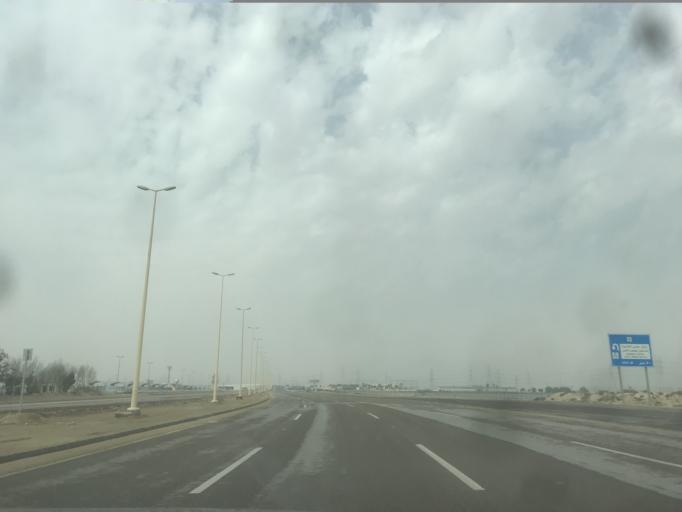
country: SA
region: Eastern Province
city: Dhahran
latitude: 26.2026
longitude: 50.0381
